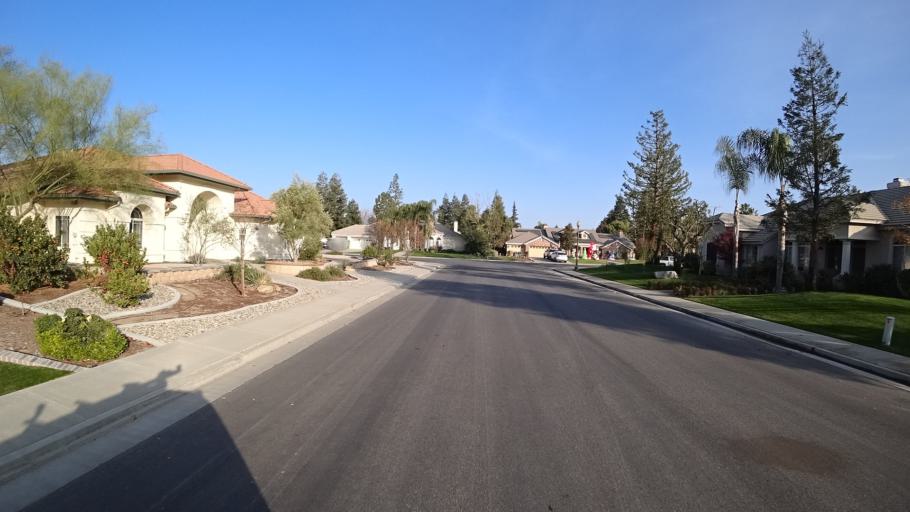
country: US
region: California
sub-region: Kern County
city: Rosedale
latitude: 35.3717
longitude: -119.1388
